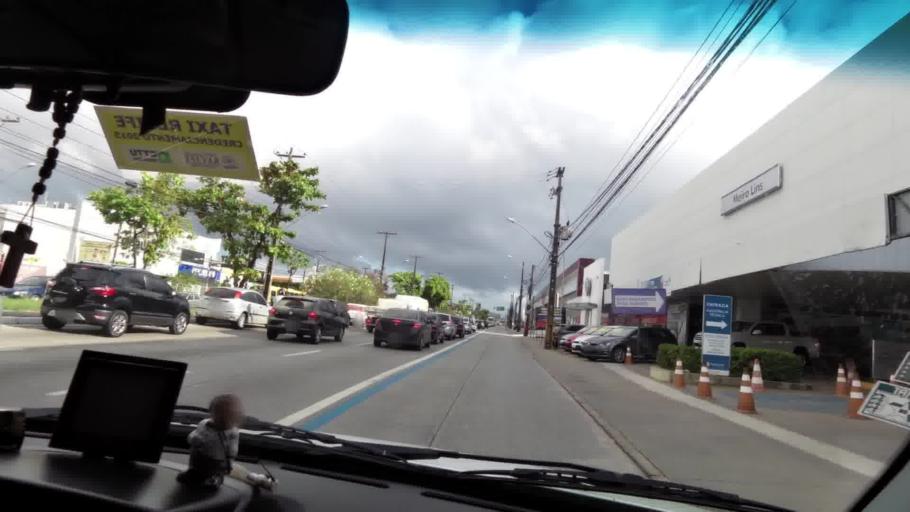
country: BR
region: Pernambuco
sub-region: Recife
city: Recife
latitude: -8.0910
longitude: -34.9086
